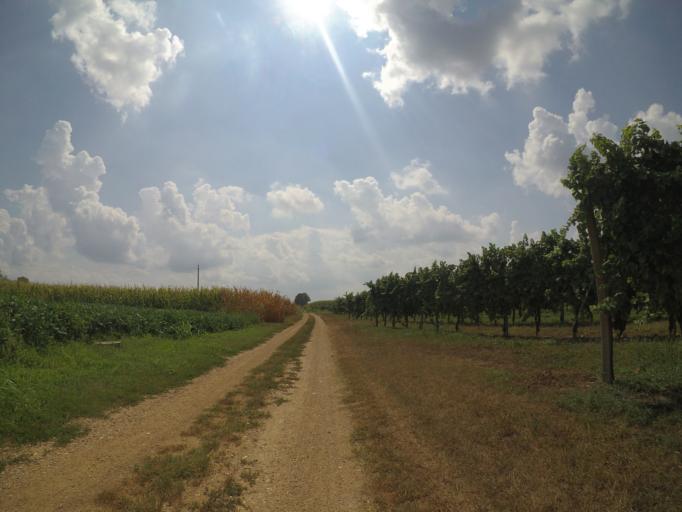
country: IT
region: Friuli Venezia Giulia
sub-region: Provincia di Udine
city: Bertiolo
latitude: 45.9690
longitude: 13.0477
